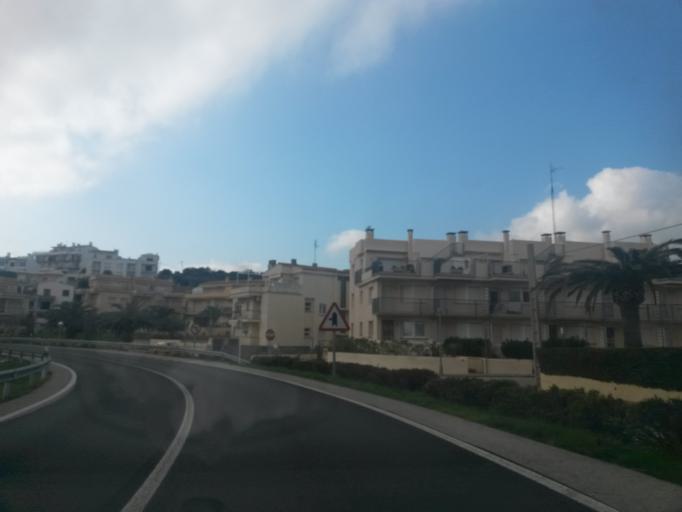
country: ES
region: Catalonia
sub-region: Provincia de Girona
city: Llanca
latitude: 42.3819
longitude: 3.1548
